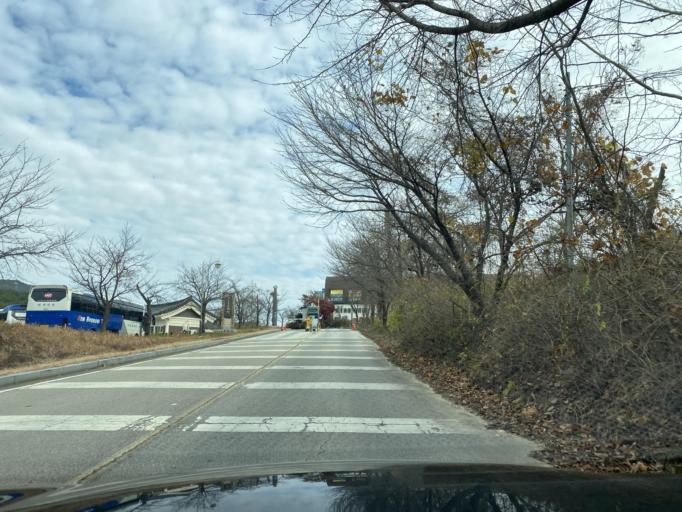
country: KR
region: Chungcheongnam-do
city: Hongsung
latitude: 36.6552
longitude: 126.6202
